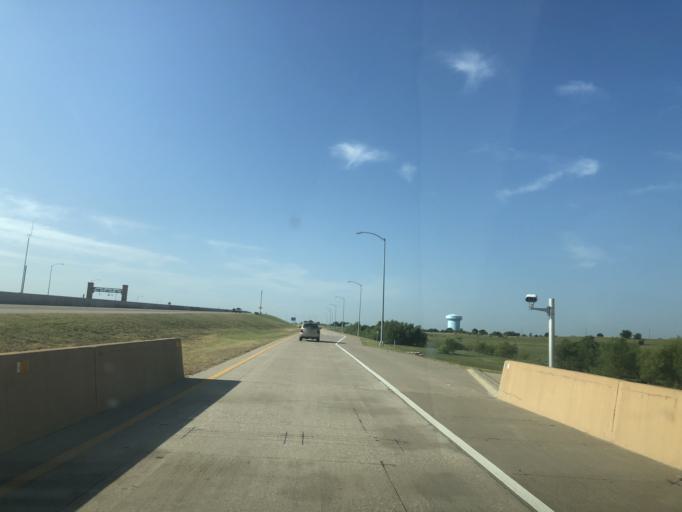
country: US
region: Texas
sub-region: Tarrant County
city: Crowley
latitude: 32.6109
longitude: -97.4130
